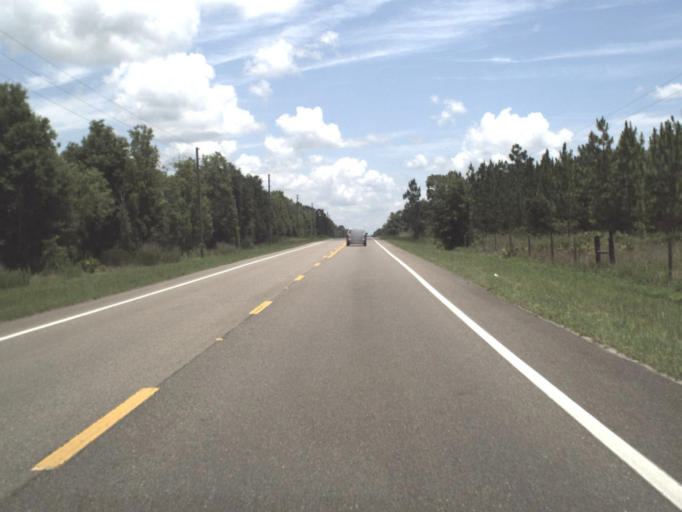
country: US
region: Florida
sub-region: Alachua County
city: Archer
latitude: 29.5067
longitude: -82.5653
